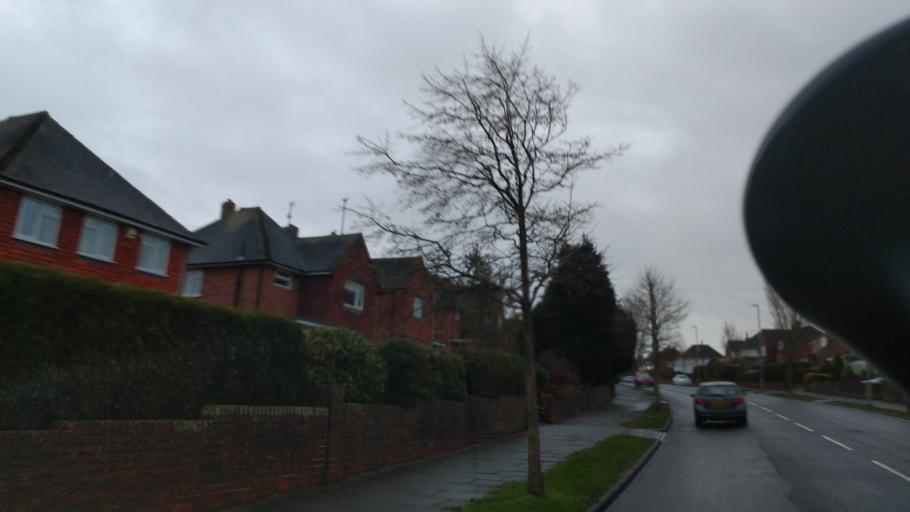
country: GB
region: England
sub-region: East Sussex
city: Eastbourne
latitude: 50.7880
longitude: 0.2560
